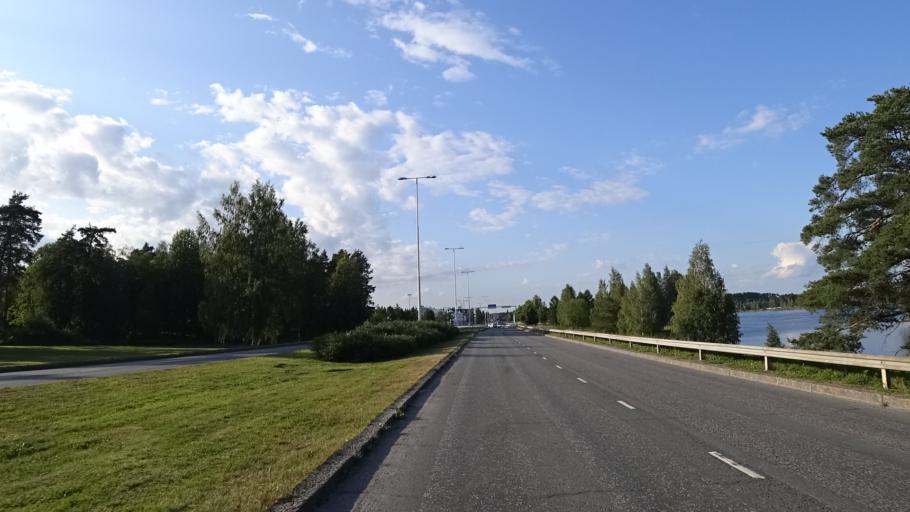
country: FI
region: South Karelia
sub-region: Imatra
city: Imatra
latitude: 61.1868
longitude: 28.7780
